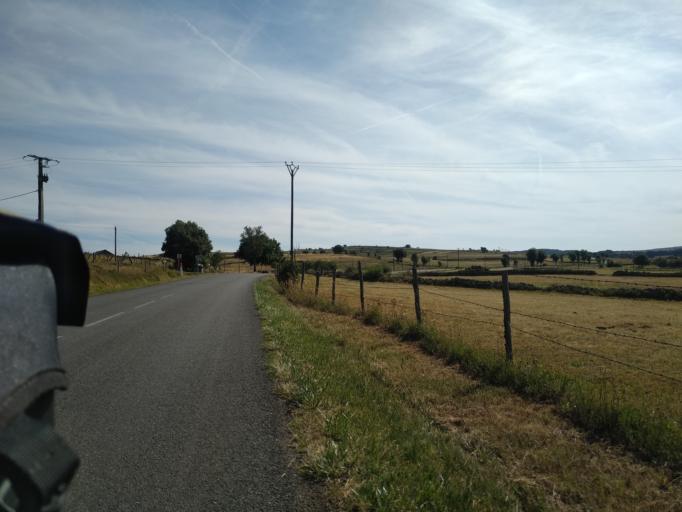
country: FR
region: Auvergne
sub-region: Departement du Cantal
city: Chaudes-Aigues
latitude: 44.6768
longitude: 3.0709
